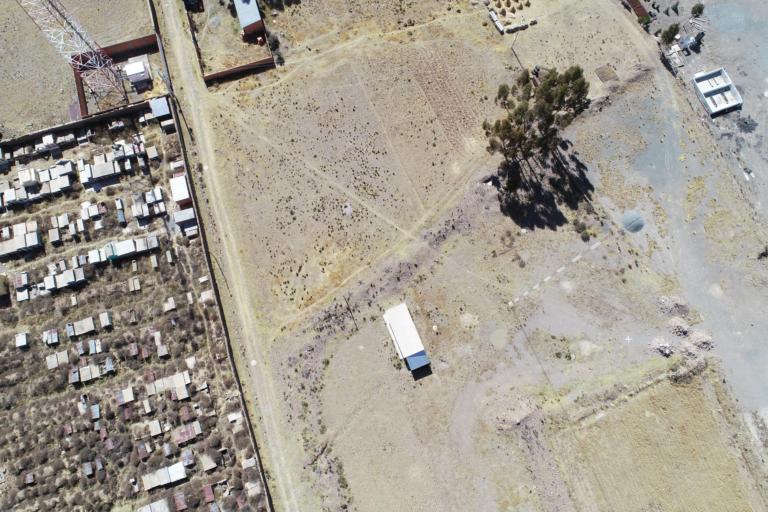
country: BO
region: La Paz
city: Achacachi
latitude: -15.9005
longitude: -68.9058
